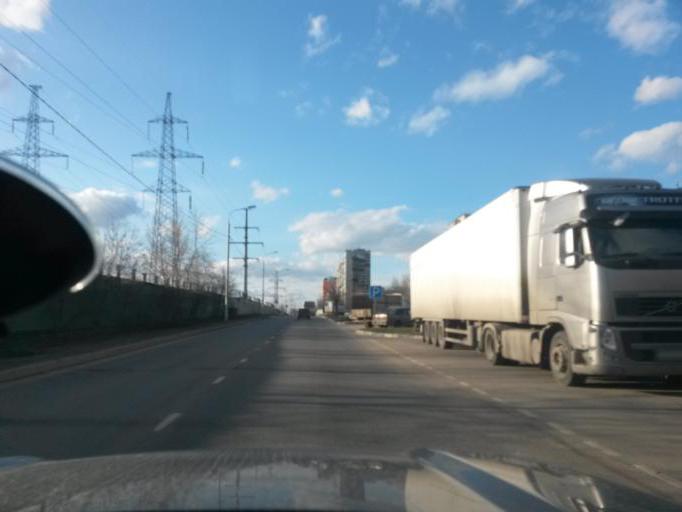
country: RU
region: Moskovskaya
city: Biryulevo Zapadnoye
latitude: 55.5772
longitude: 37.6436
